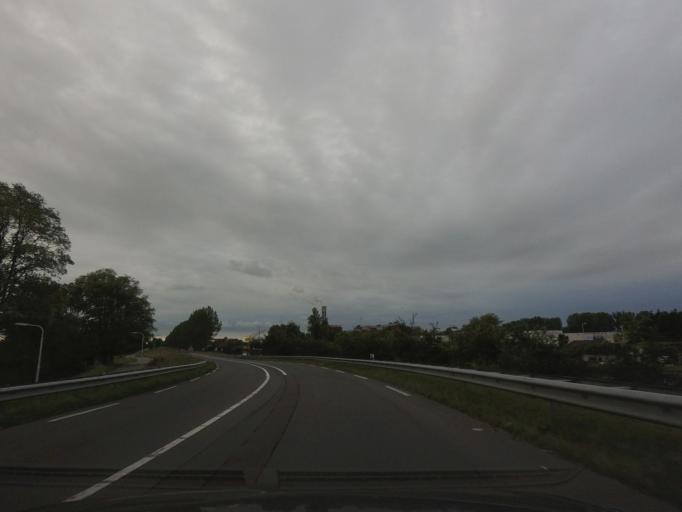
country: NL
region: North Holland
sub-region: Gemeente Alkmaar
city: Alkmaar
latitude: 52.6156
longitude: 4.7686
